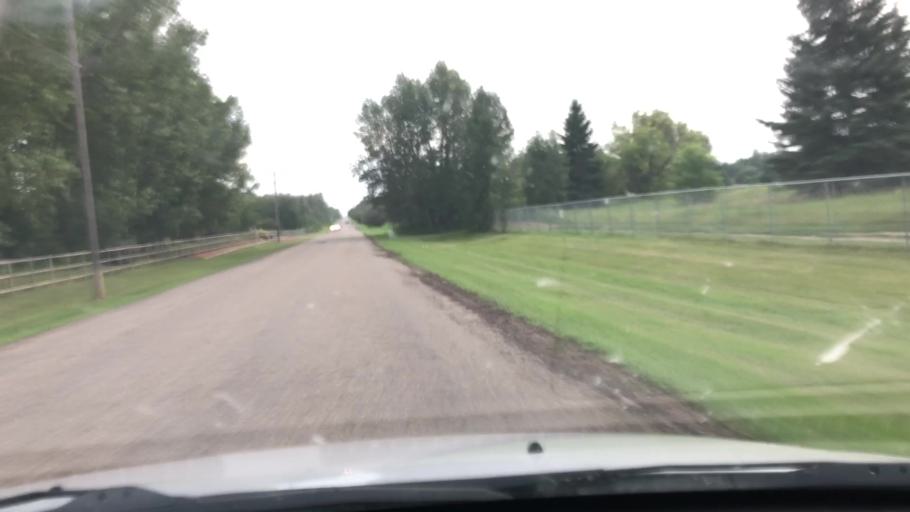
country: CA
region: Alberta
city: Devon
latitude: 53.4172
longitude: -113.6892
